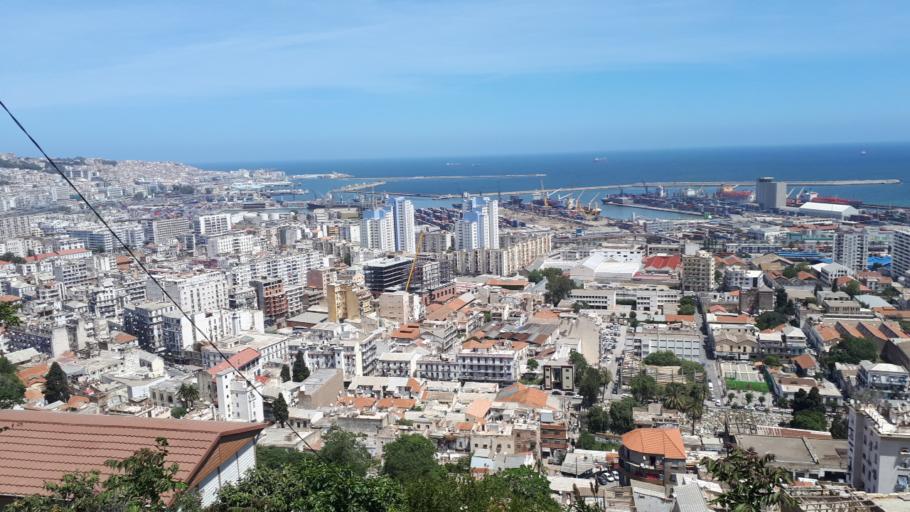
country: DZ
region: Alger
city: Algiers
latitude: 36.7482
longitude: 3.0634
